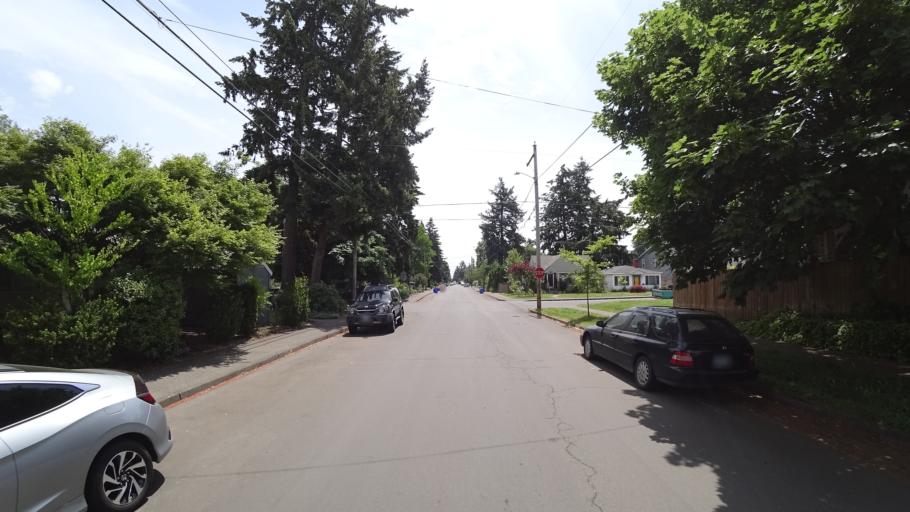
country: US
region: Oregon
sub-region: Multnomah County
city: Lents
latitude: 45.4785
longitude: -122.5996
